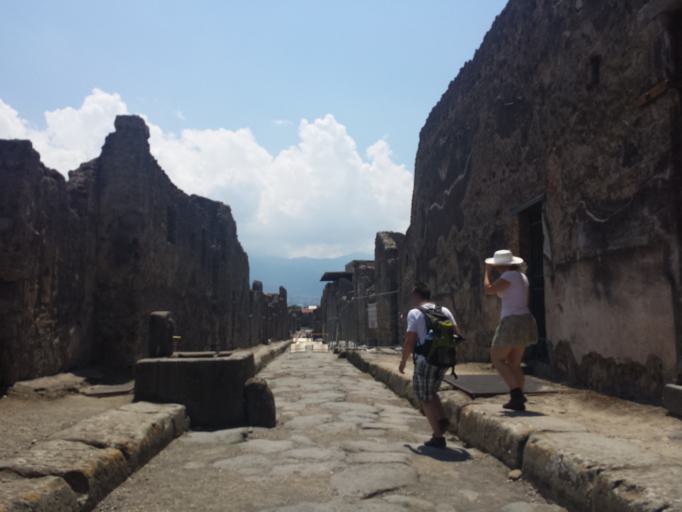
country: IT
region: Campania
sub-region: Provincia di Napoli
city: Pompei
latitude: 40.7528
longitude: 14.4844
